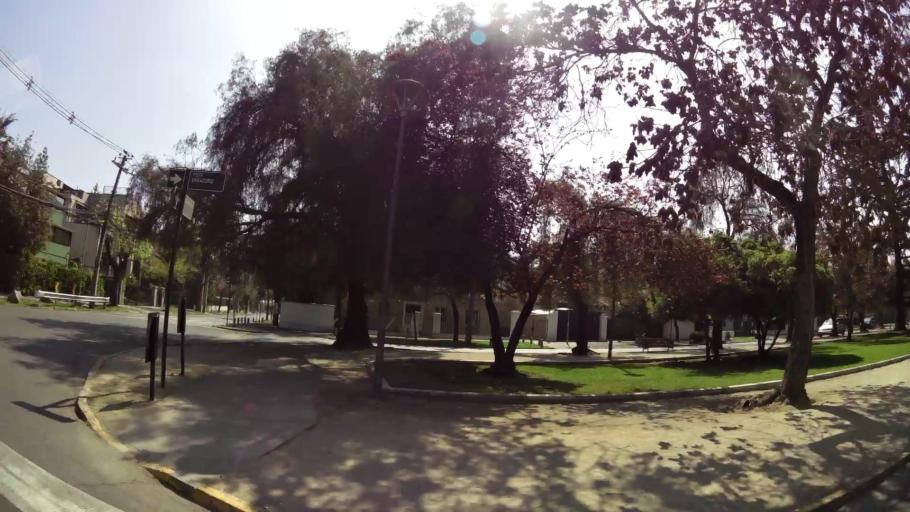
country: CL
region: Santiago Metropolitan
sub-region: Provincia de Santiago
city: Villa Presidente Frei, Nunoa, Santiago, Chile
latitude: -33.4212
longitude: -70.5933
